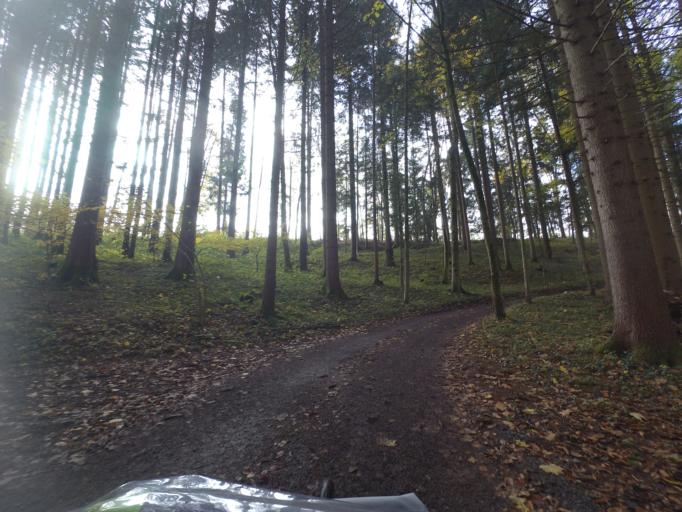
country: AT
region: Salzburg
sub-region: Politischer Bezirk Hallein
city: Adnet
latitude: 47.6733
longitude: 13.1450
